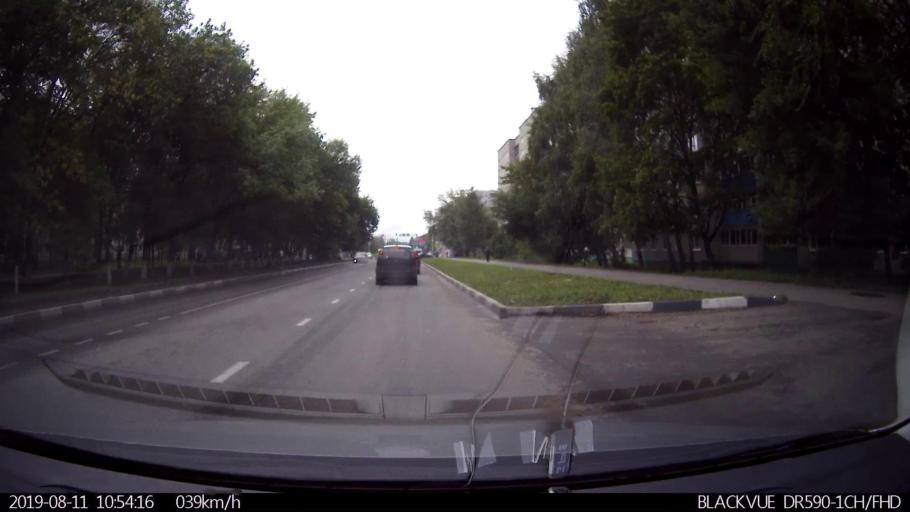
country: RU
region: Ulyanovsk
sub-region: Ulyanovskiy Rayon
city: Ulyanovsk
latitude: 54.2572
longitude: 48.3342
